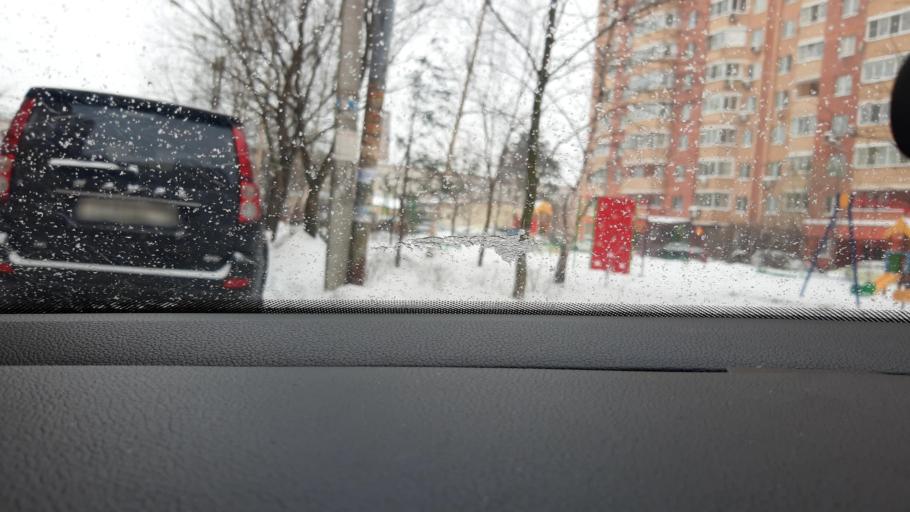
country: RU
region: Moskovskaya
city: Yubileyny
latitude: 55.9306
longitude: 37.8313
